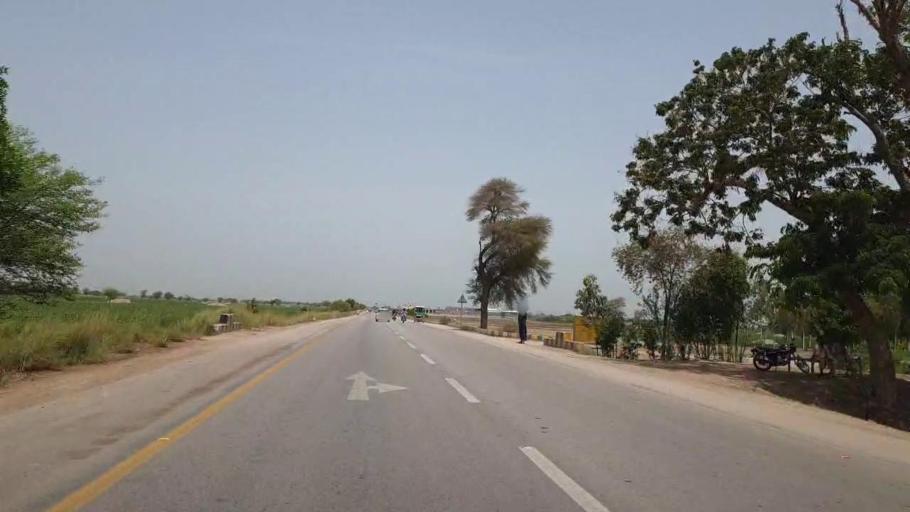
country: PK
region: Sindh
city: Nawabshah
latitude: 26.2271
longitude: 68.4904
